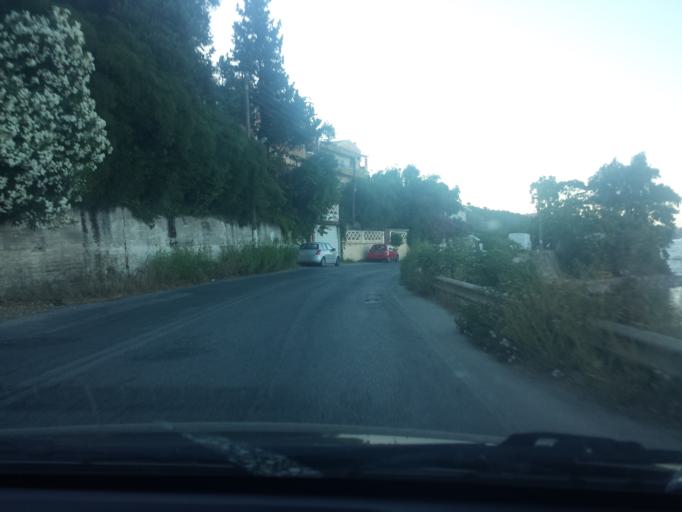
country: GR
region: Ionian Islands
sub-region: Nomos Kerkyras
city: Perama
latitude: 39.5602
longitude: 19.9108
